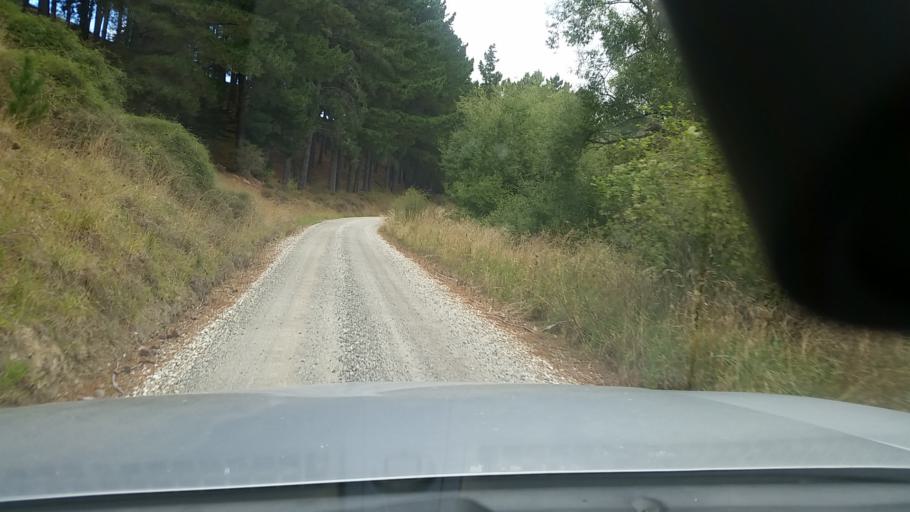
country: NZ
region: Marlborough
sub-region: Marlborough District
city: Blenheim
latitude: -41.6904
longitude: 174.1262
